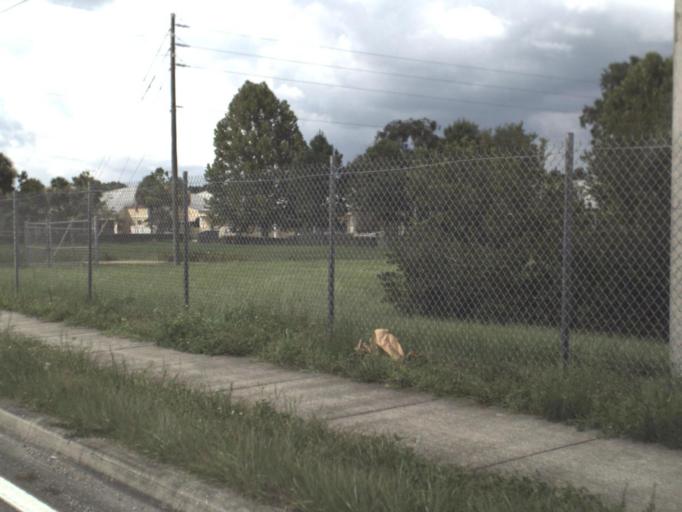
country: US
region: Florida
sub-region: Hillsborough County
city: Lutz
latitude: 28.1787
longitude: -82.4645
